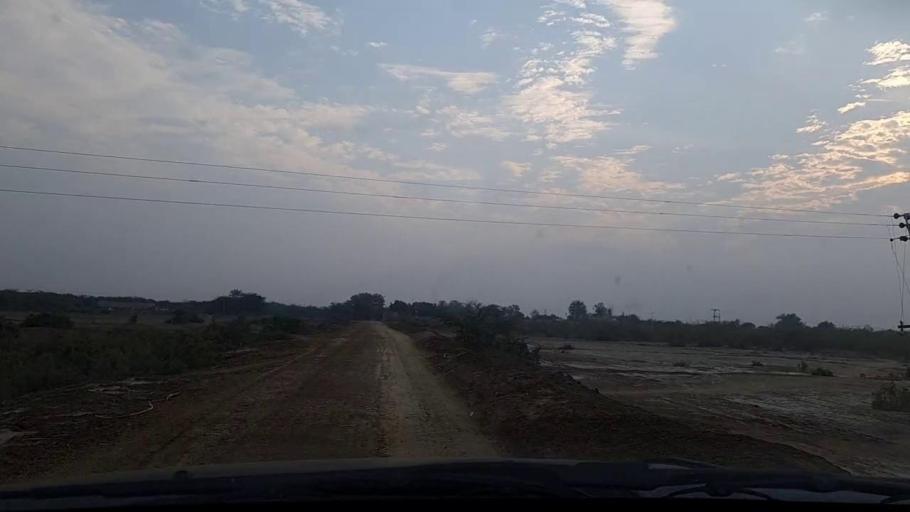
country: PK
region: Sindh
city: Pithoro
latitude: 25.6261
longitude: 69.4162
